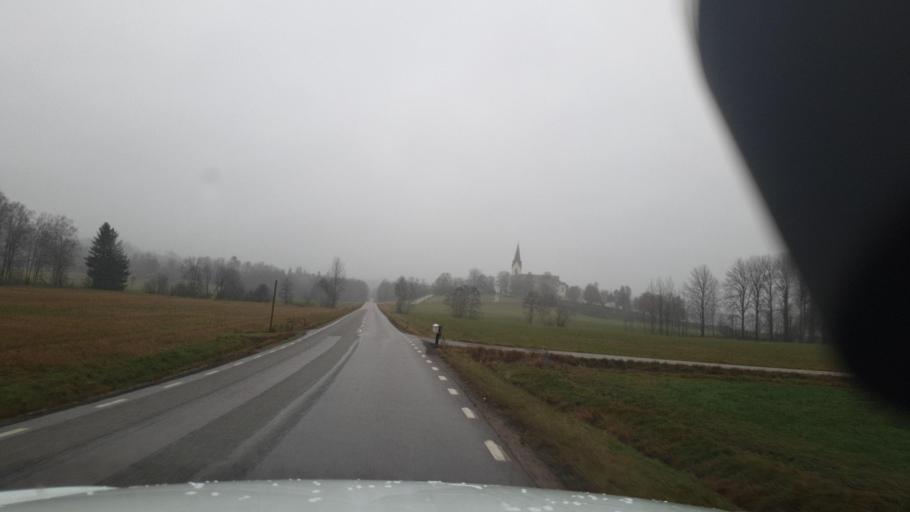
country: SE
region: Vaermland
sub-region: Arvika Kommun
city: Arvika
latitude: 59.6482
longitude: 12.8929
